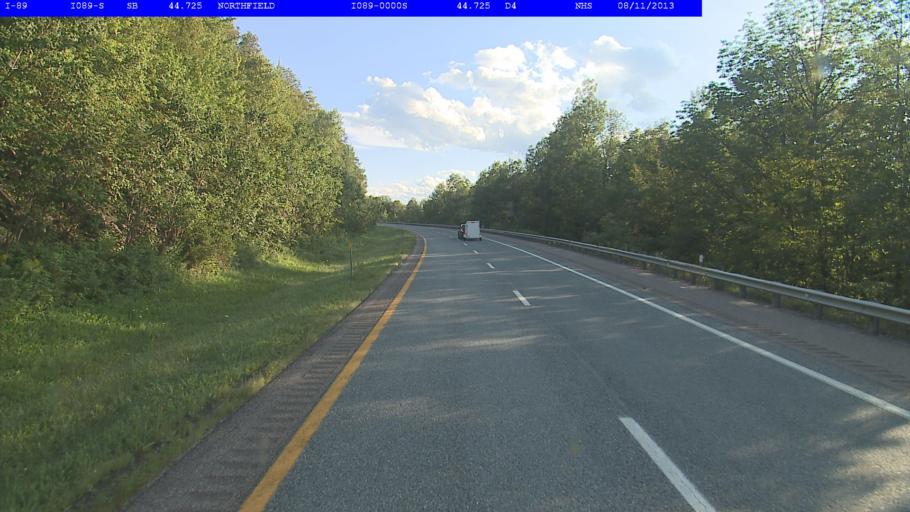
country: US
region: Vermont
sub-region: Washington County
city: Northfield
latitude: 44.1399
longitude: -72.5996
